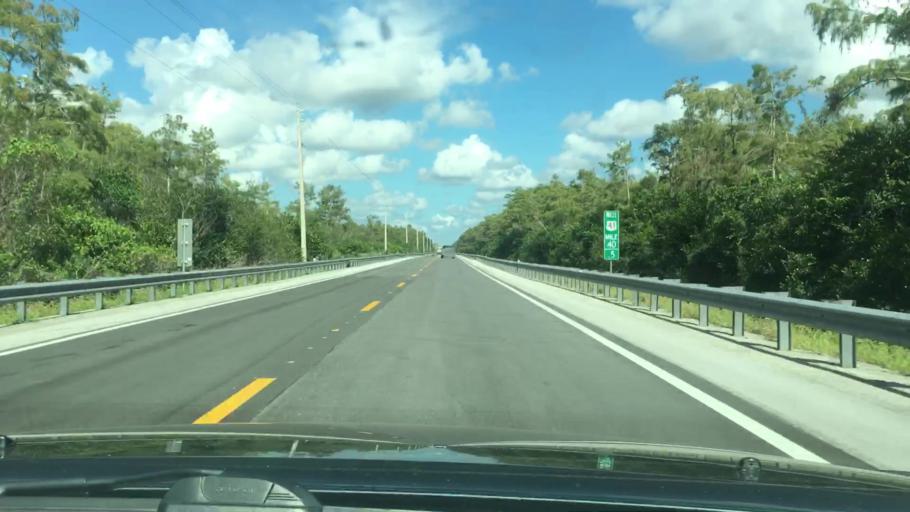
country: US
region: Florida
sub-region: Miami-Dade County
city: Kendall West
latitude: 25.7705
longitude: -80.8371
